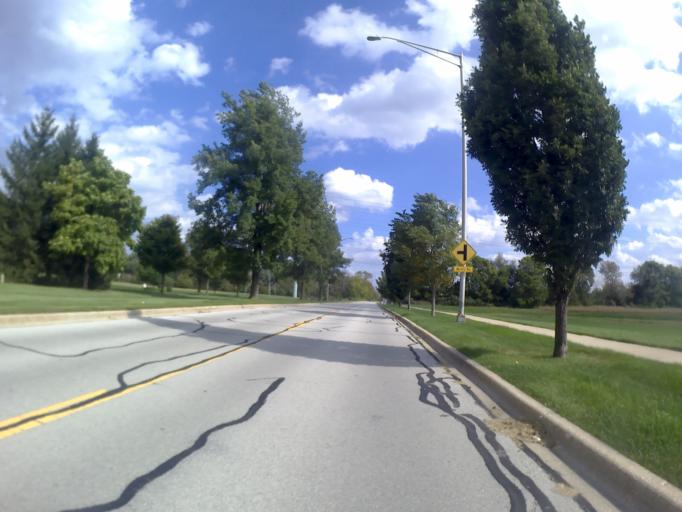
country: US
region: Illinois
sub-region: Will County
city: Bolingbrook
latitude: 41.7272
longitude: -88.0989
